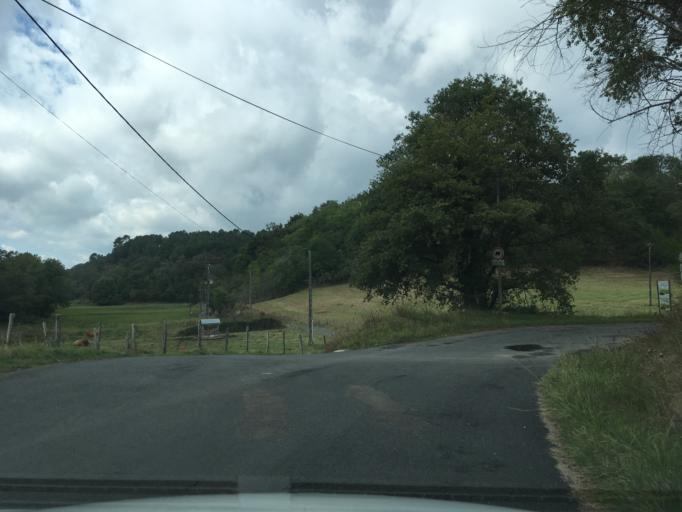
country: FR
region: Limousin
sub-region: Departement de la Correze
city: Brive-la-Gaillarde
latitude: 45.1190
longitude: 1.5515
